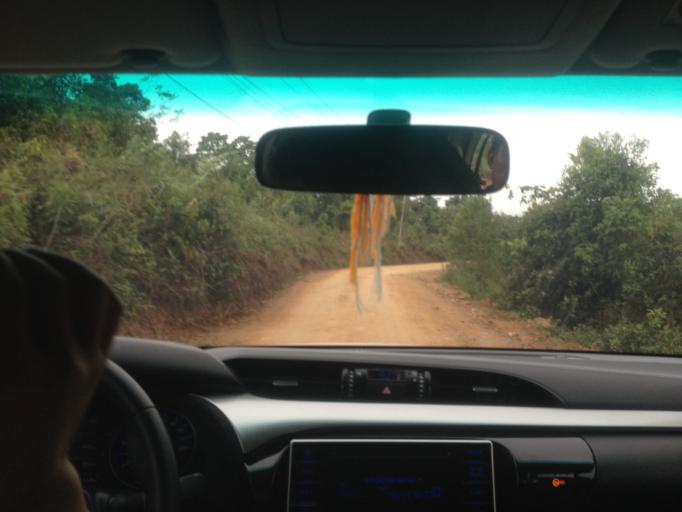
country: TH
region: Nan
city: Chaloem Phra Kiat
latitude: 19.9949
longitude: 101.1348
